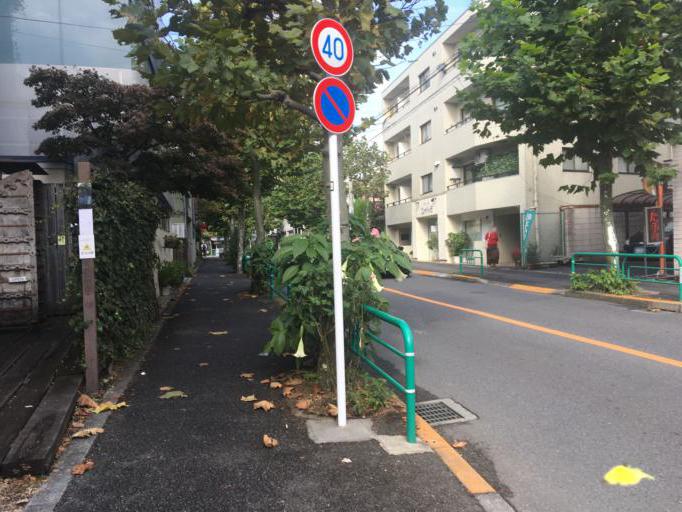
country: JP
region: Tokyo
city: Musashino
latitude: 35.7098
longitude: 139.6019
